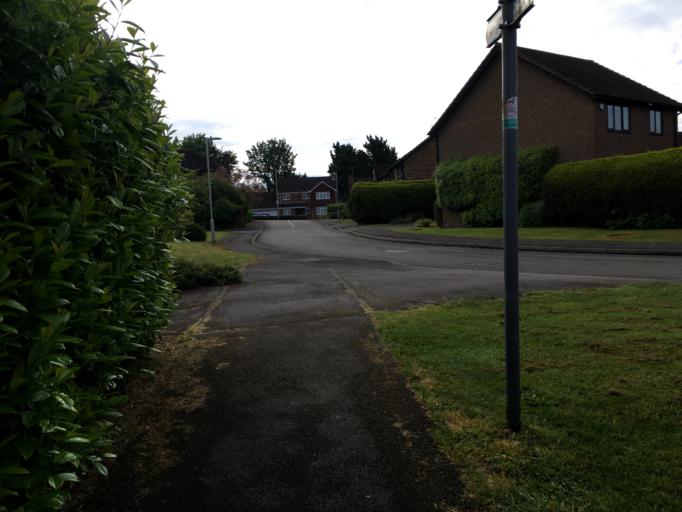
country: GB
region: England
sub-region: West Berkshire
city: Calcot
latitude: 51.4421
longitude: -1.0398
